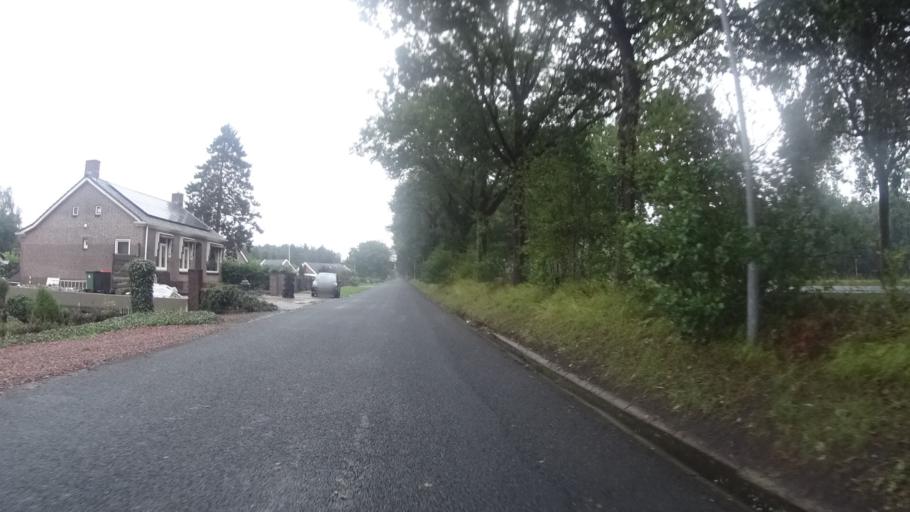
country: NL
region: Groningen
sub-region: Gemeente  Oldambt
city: Winschoten
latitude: 53.1705
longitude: 6.9851
